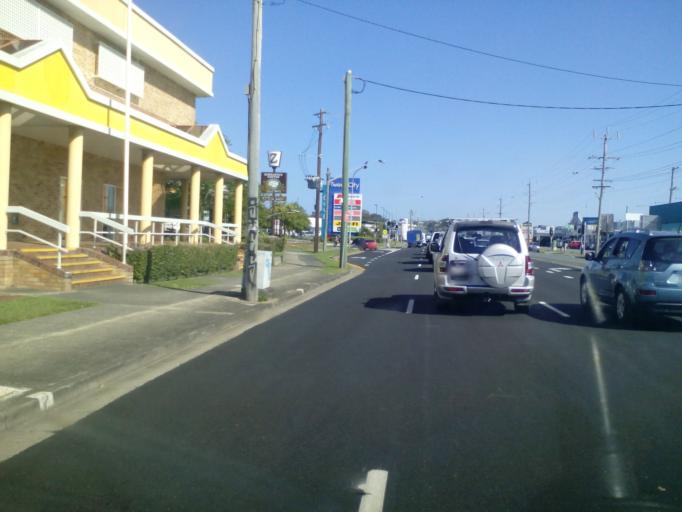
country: AU
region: New South Wales
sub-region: Tweed
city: Banora Point
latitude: -28.1991
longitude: 153.5439
